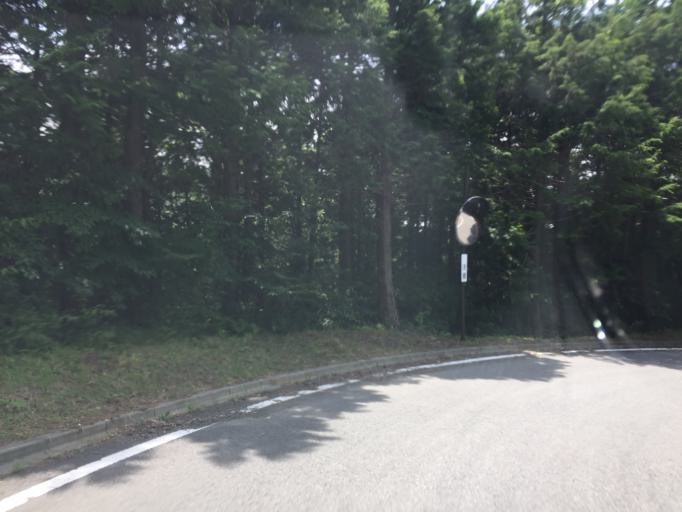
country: JP
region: Fukushima
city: Yanagawamachi-saiwaicho
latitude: 37.7489
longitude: 140.7302
